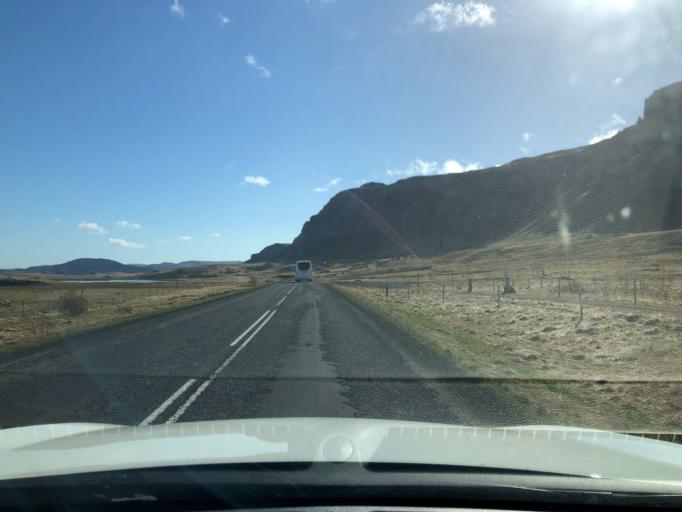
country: IS
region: West
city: Borgarnes
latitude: 64.5314
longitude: -21.7947
